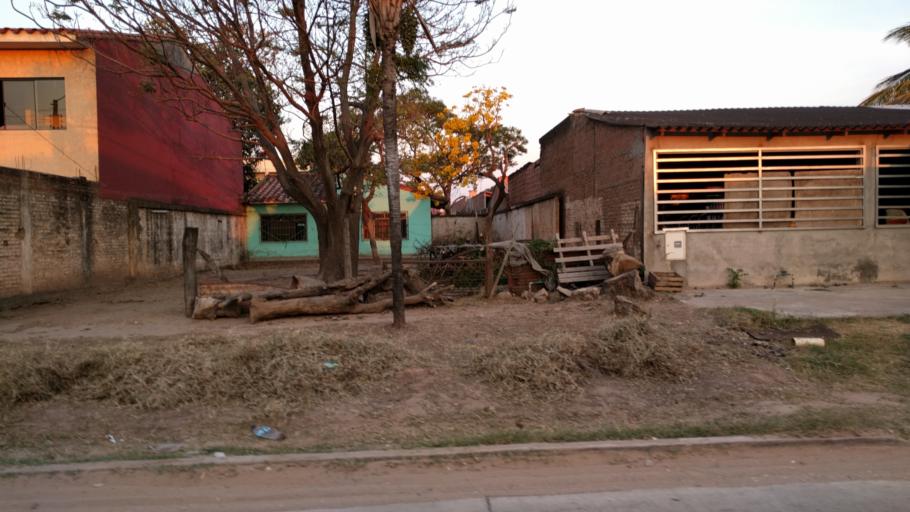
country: BO
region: Santa Cruz
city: Santa Cruz de la Sierra
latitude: -17.7498
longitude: -63.1478
